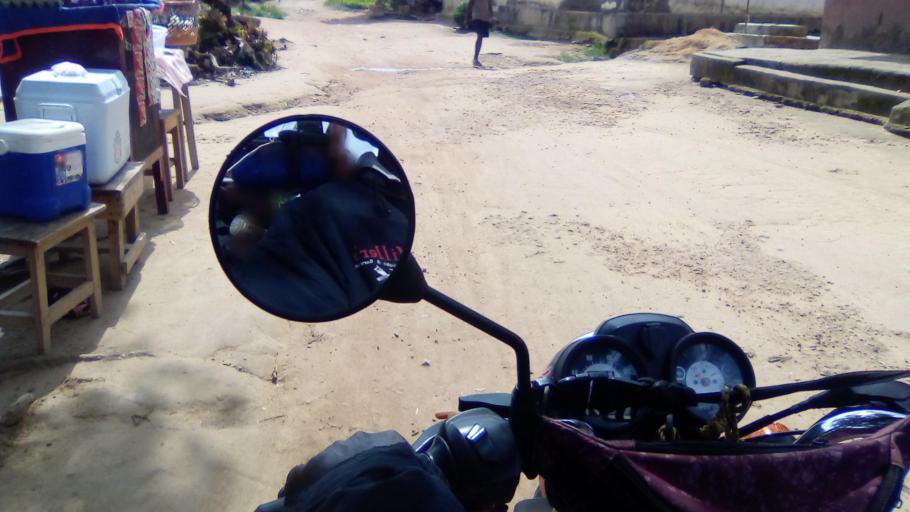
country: SL
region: Southern Province
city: Bo
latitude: 7.9493
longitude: -11.7240
